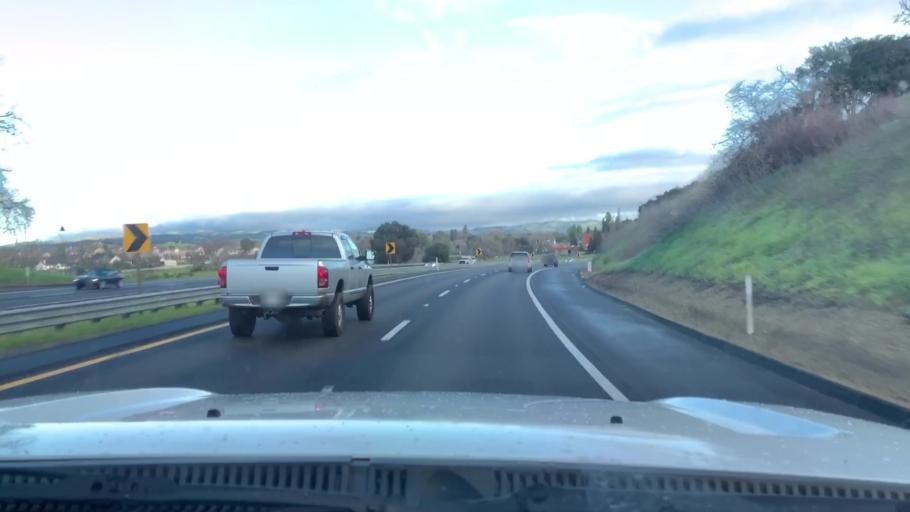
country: US
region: California
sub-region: San Luis Obispo County
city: Templeton
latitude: 35.5470
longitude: -120.7163
